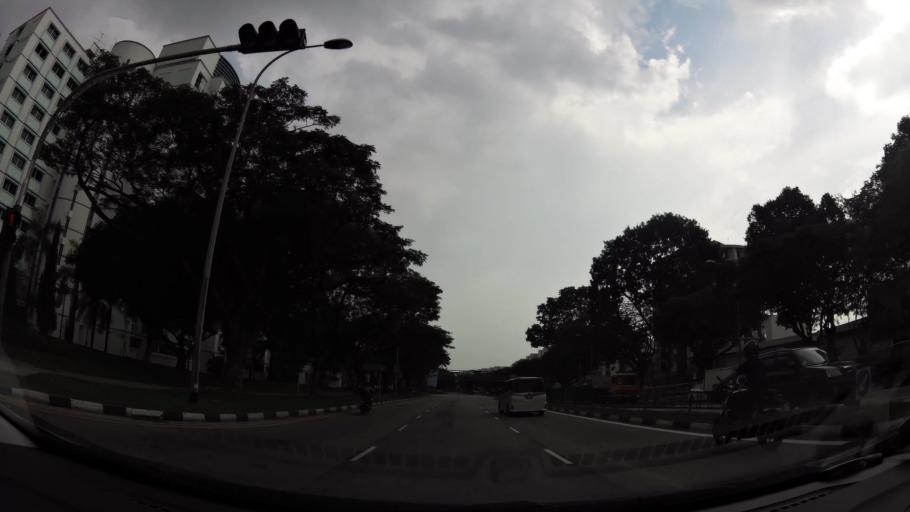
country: SG
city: Singapore
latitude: 1.3489
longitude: 103.9287
